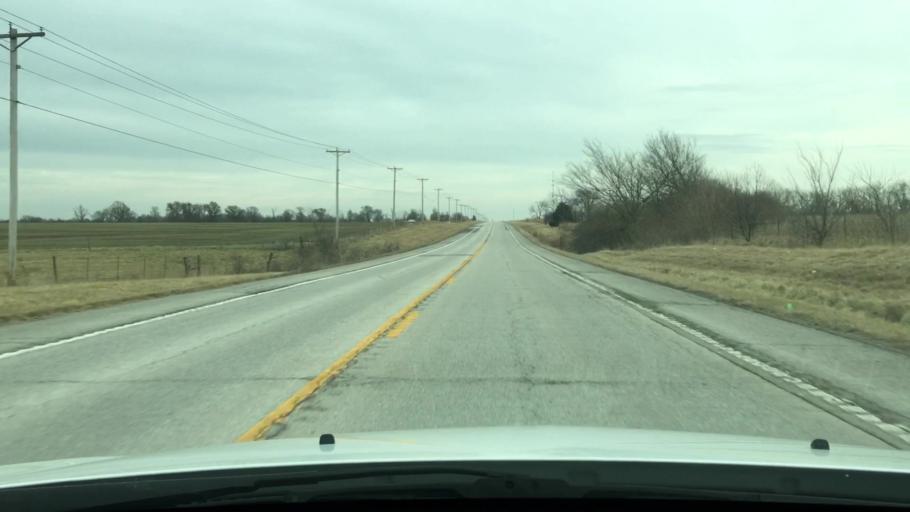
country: US
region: Missouri
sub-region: Pike County
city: Bowling Green
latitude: 39.3451
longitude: -91.3298
